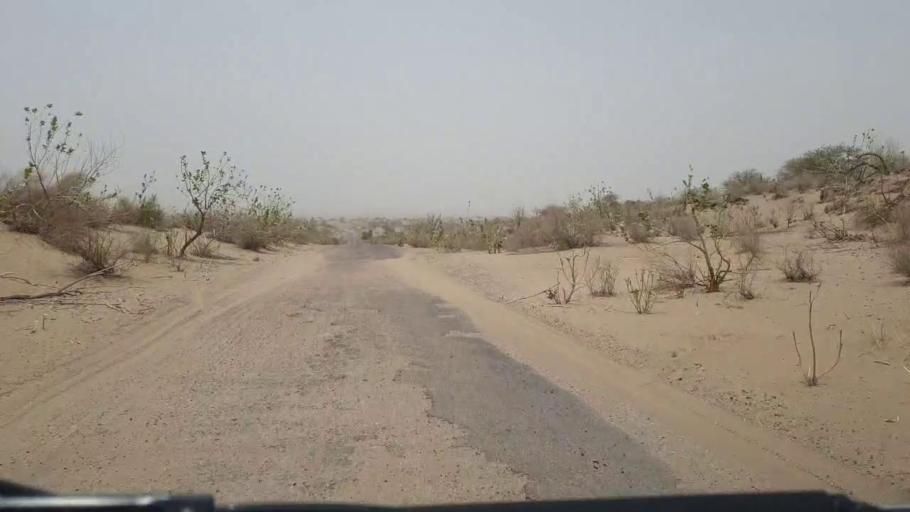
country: PK
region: Sindh
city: Naukot
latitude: 24.7706
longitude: 69.5375
